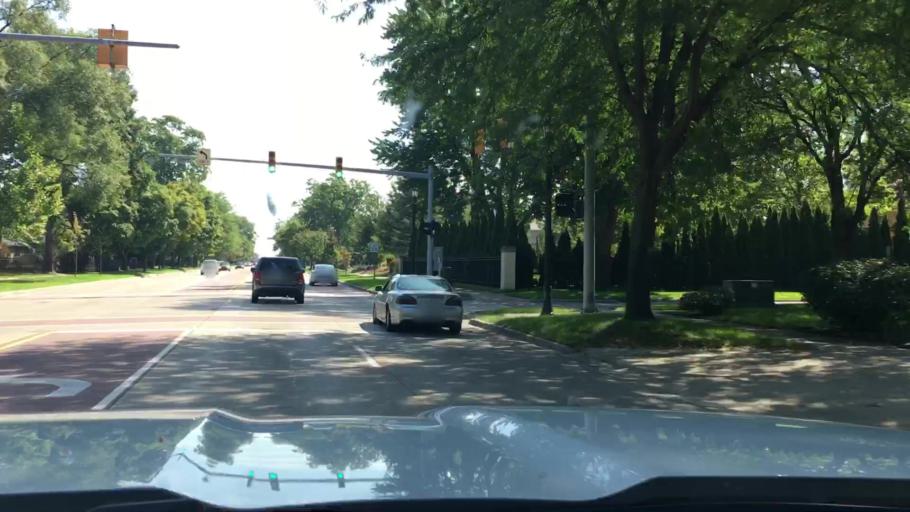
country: US
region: Michigan
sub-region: Bay County
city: Bay City
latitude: 43.5960
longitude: -83.8628
